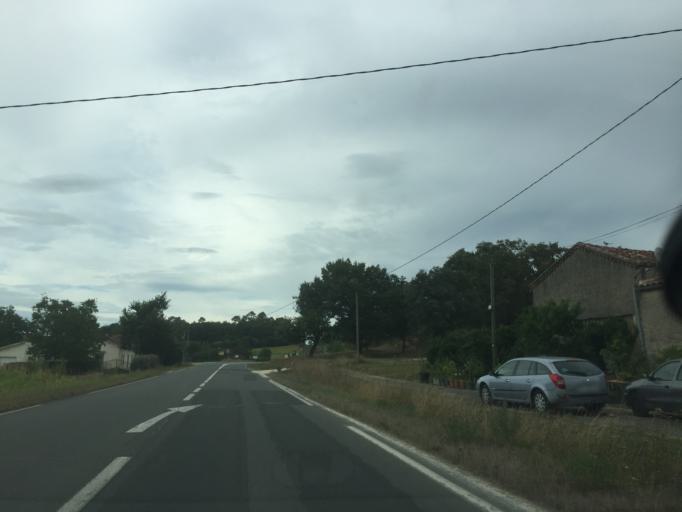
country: FR
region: Aquitaine
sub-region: Departement du Lot-et-Garonne
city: Fumel
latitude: 44.5206
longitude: 0.9483
